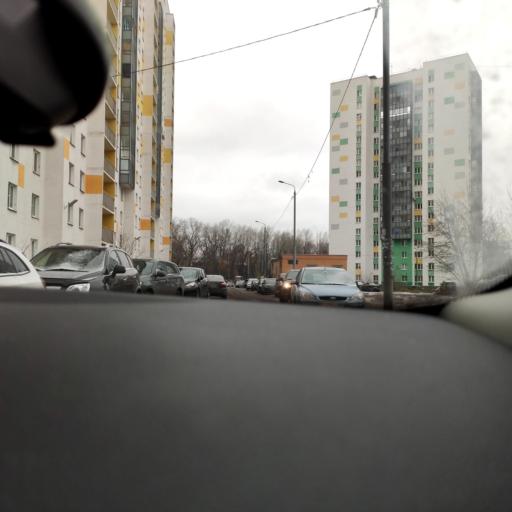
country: RU
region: Moskovskaya
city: Mytishchi
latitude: 55.9223
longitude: 37.7457
